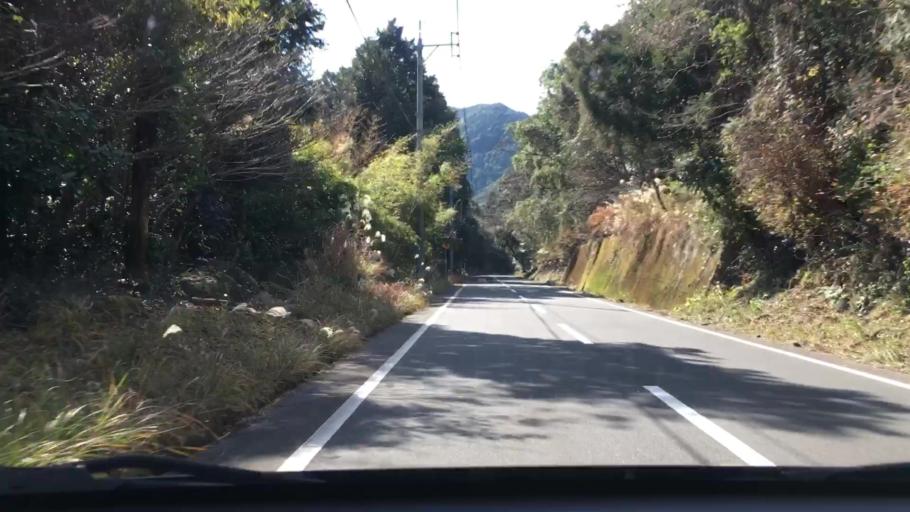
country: JP
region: Kagoshima
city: Ijuin
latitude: 31.7146
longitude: 130.4254
